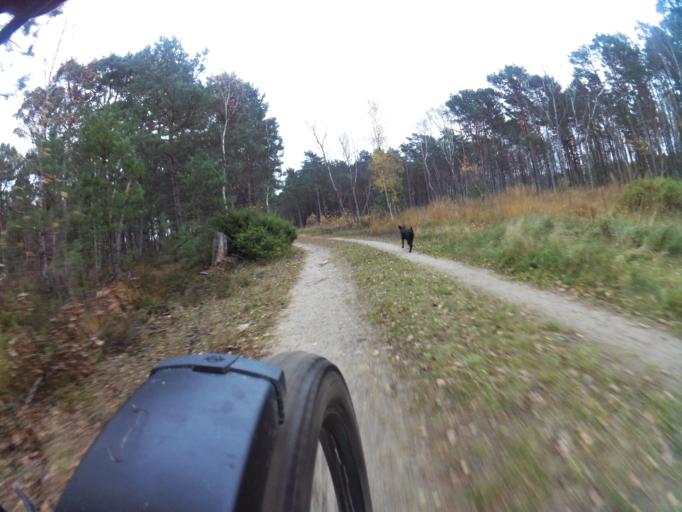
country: PL
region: Pomeranian Voivodeship
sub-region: Powiat leborski
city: Leba
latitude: 54.7784
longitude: 17.7186
